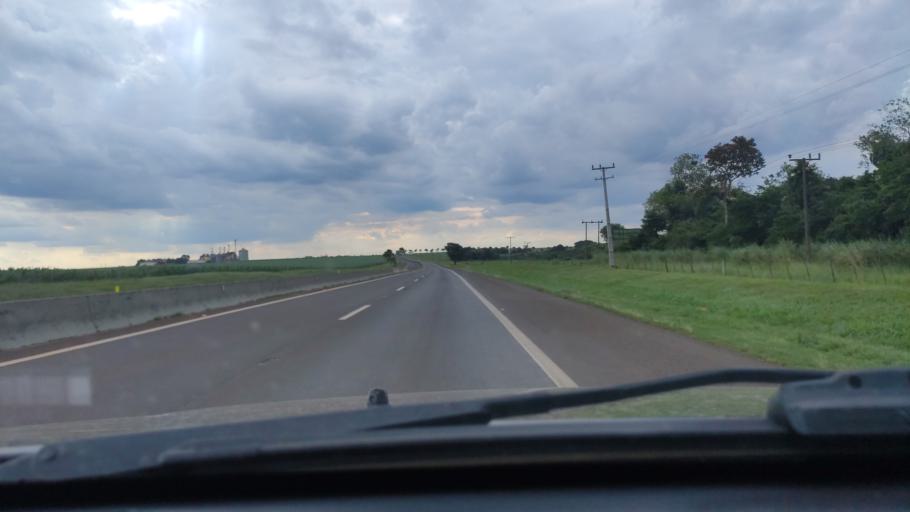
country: BR
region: Sao Paulo
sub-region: Palmital
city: Palmital
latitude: -22.8308
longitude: -50.0273
